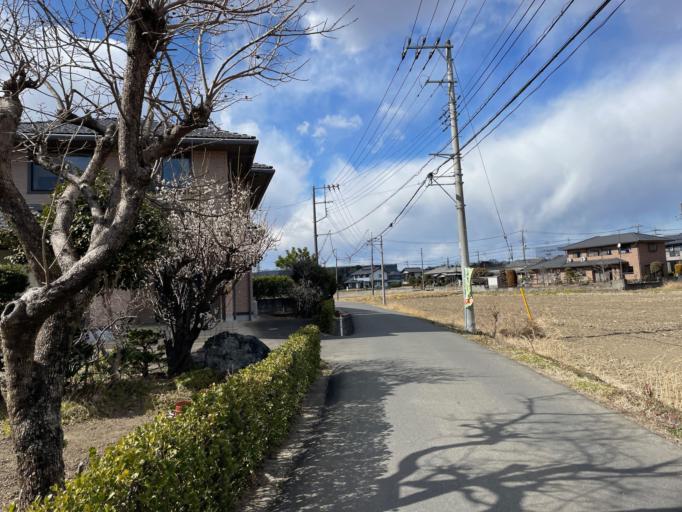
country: JP
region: Saitama
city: Sakado
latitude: 36.0232
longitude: 139.3803
